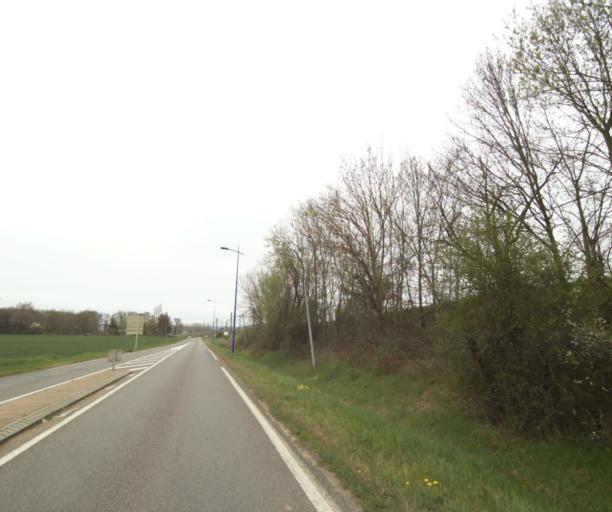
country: FR
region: Bourgogne
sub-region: Departement de Saone-et-Loire
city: Charnay-les-Macon
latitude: 46.2847
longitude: 4.7759
